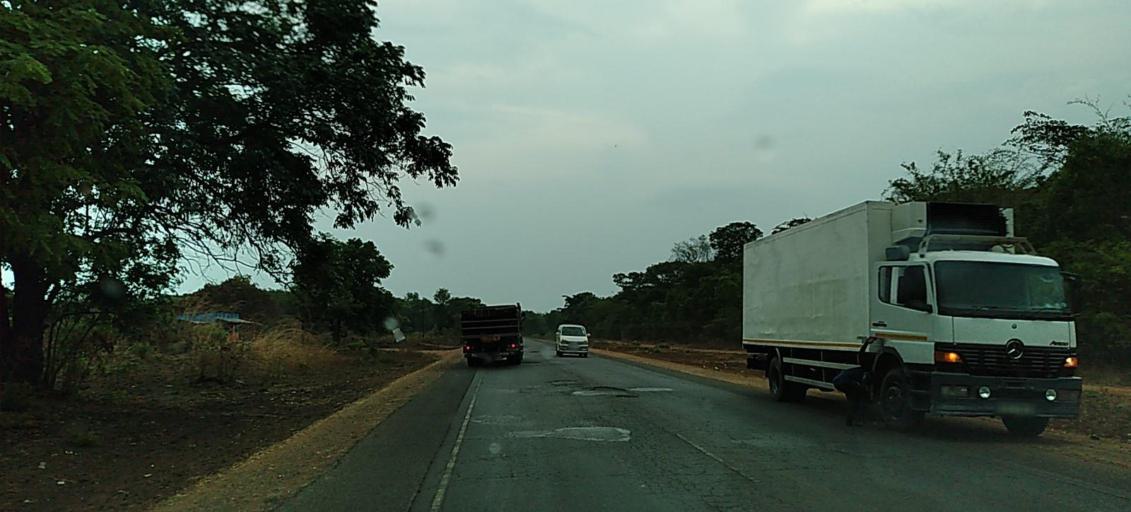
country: ZM
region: Copperbelt
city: Luanshya
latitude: -13.0595
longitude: 28.4578
